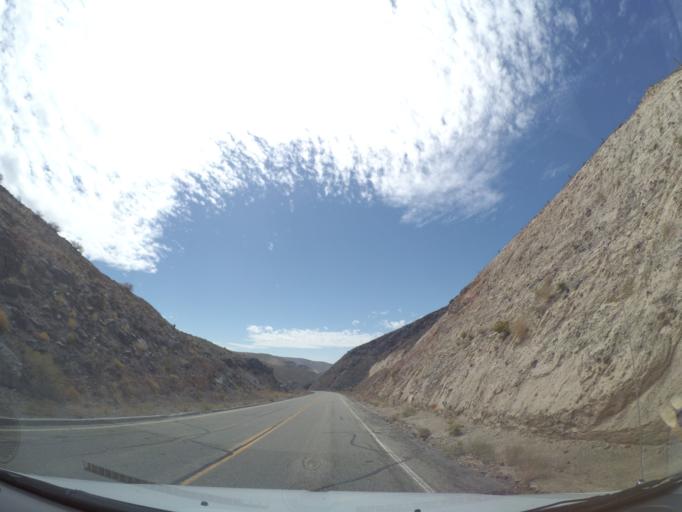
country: US
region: California
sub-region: San Bernardino County
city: Searles Valley
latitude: 36.3755
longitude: -117.2854
